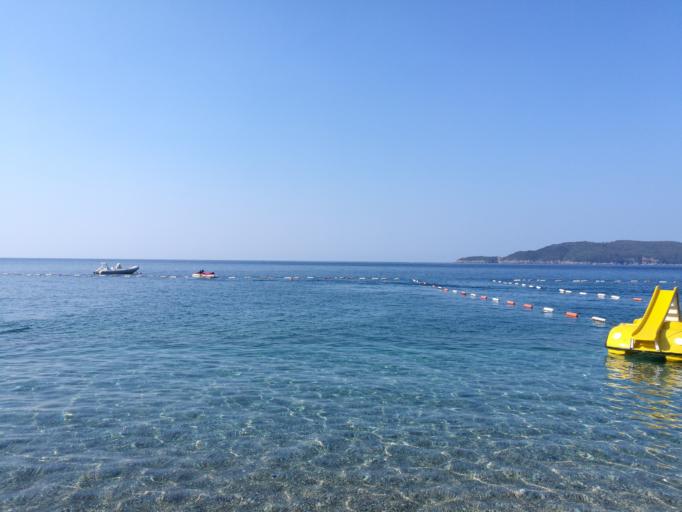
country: ME
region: Budva
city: Budva
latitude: 42.2755
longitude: 18.8864
